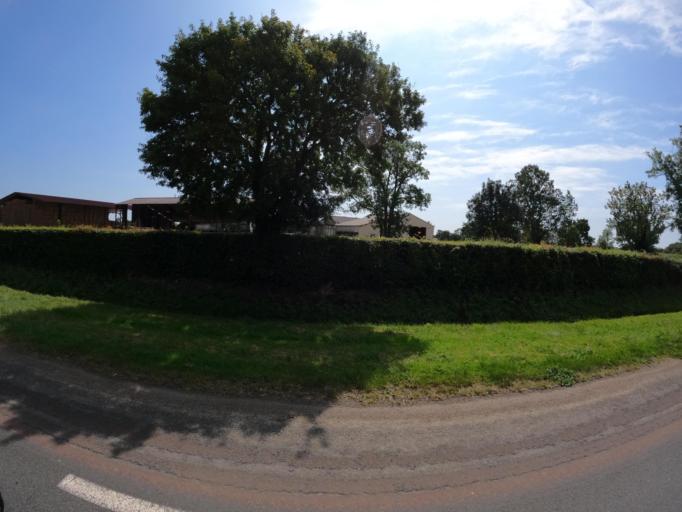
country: FR
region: Poitou-Charentes
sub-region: Departement des Deux-Sevres
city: Bessines
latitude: 46.2794
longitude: -0.5221
